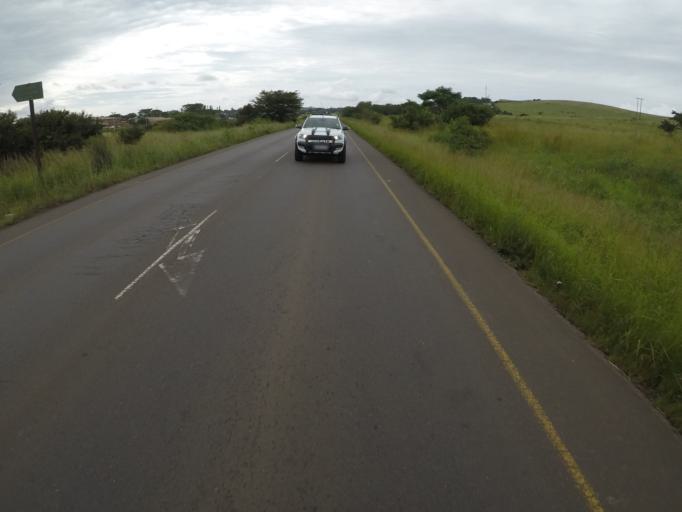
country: ZA
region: KwaZulu-Natal
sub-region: uThungulu District Municipality
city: Empangeni
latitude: -28.7326
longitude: 31.8747
